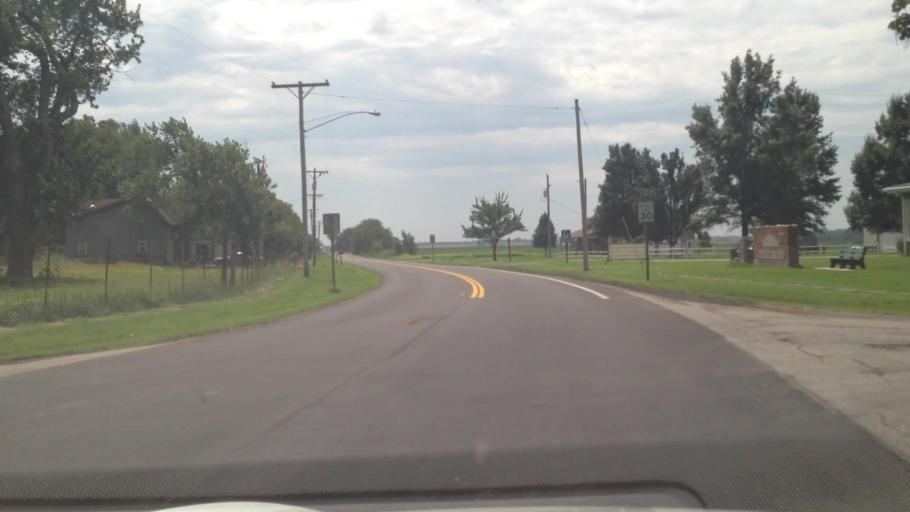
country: US
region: Kansas
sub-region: Crawford County
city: Girard
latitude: 37.6601
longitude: -94.9697
